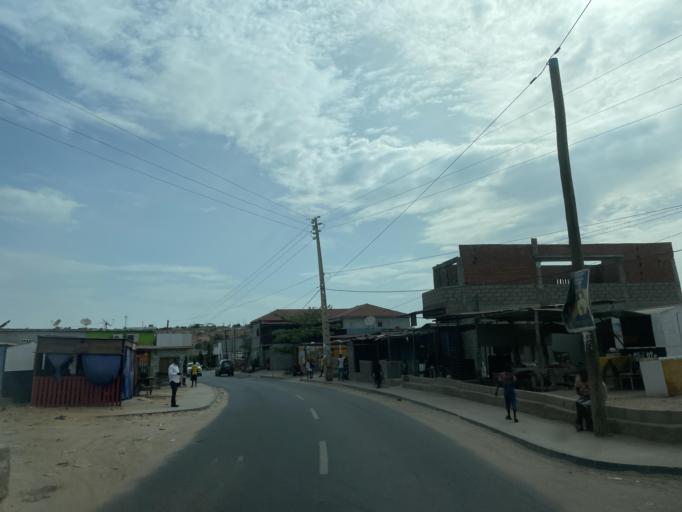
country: AO
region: Luanda
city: Luanda
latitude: -8.9351
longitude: 13.1976
